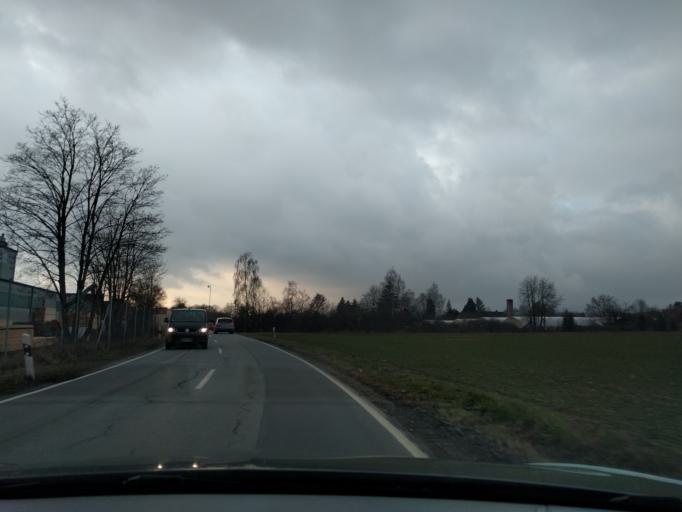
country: DE
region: Bavaria
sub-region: Lower Bavaria
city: Hengersberg
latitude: 48.7665
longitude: 13.0675
